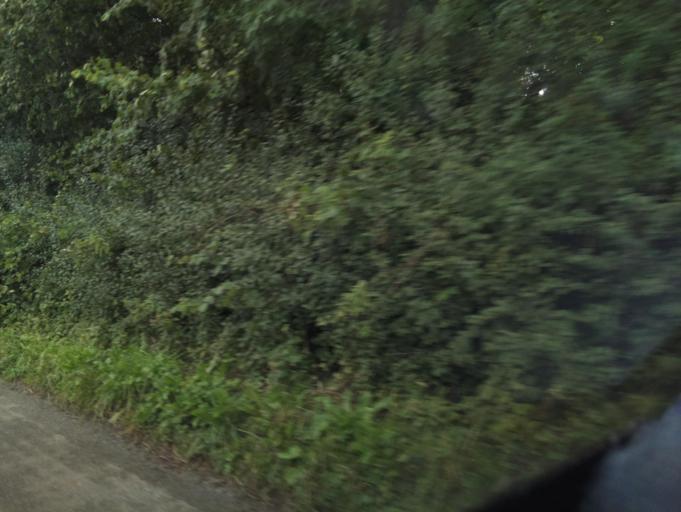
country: GB
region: England
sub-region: Somerset
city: Evercreech
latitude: 51.1684
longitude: -2.5063
